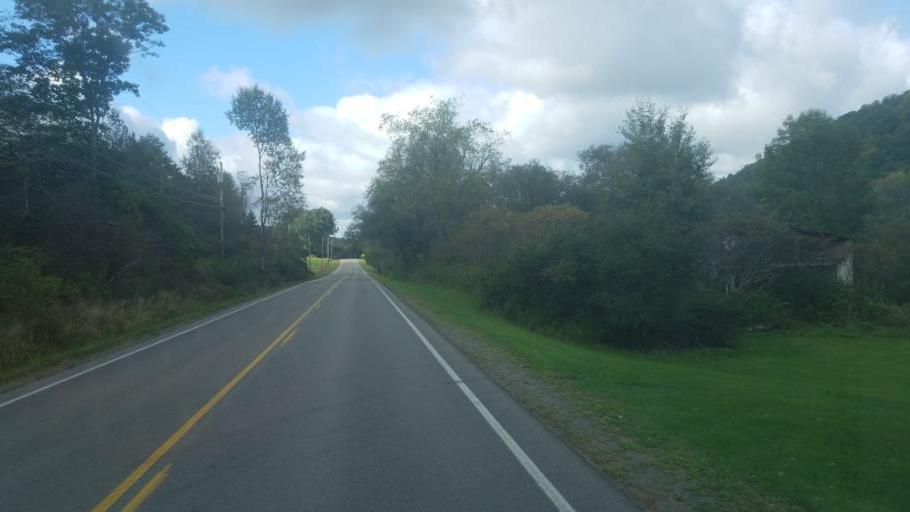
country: US
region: New York
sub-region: Allegany County
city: Cuba
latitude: 42.1501
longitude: -78.2999
